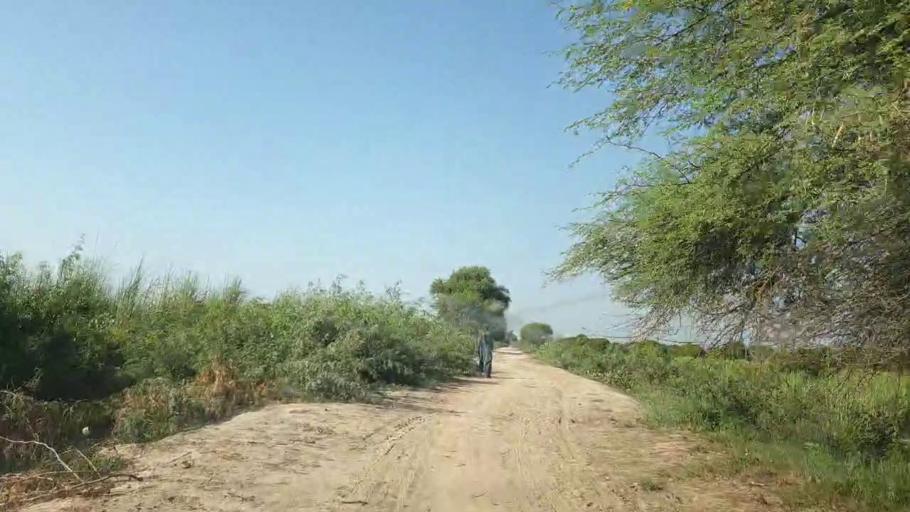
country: PK
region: Sindh
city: Tando Jam
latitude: 25.3635
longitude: 68.5695
